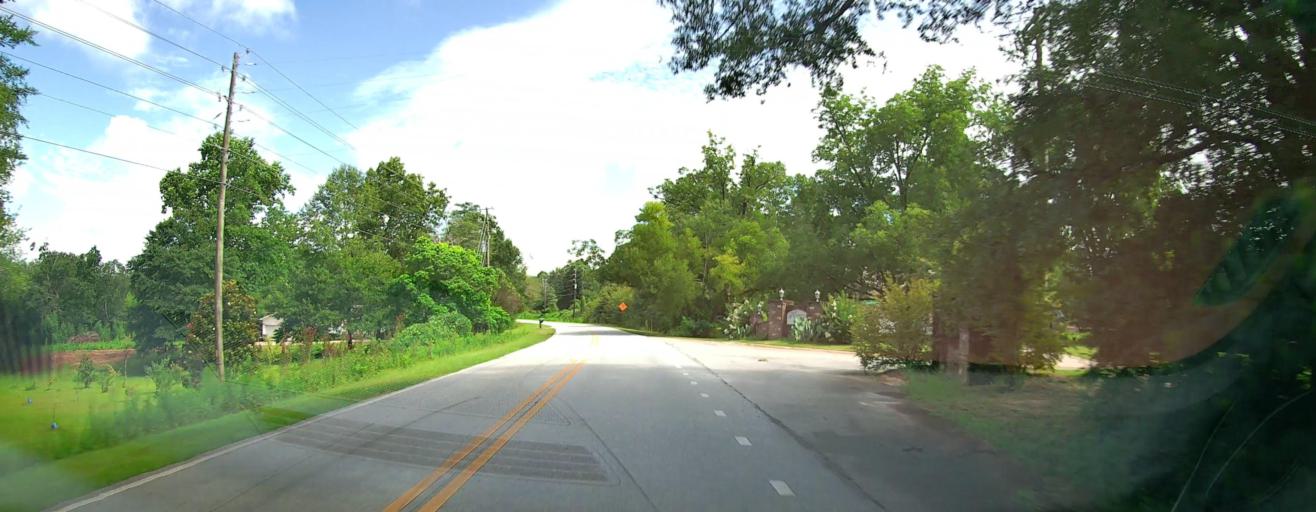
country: US
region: Georgia
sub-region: Peach County
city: Byron
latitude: 32.6177
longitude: -83.7981
